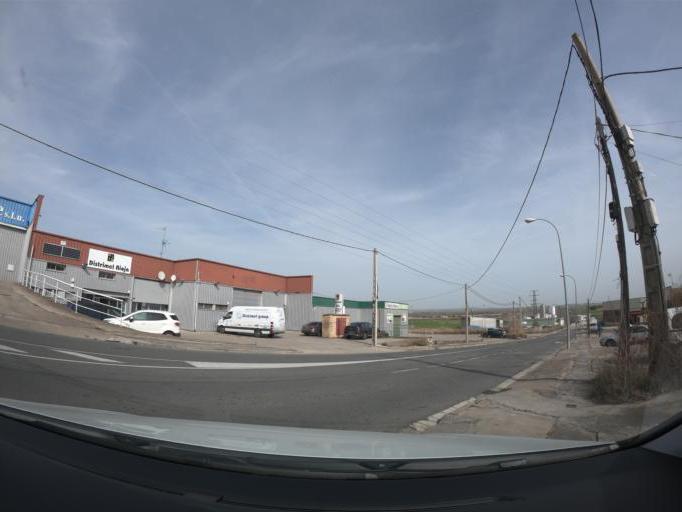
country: ES
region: Basque Country
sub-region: Provincia de Alava
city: Oyon
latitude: 42.4784
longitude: -2.4103
